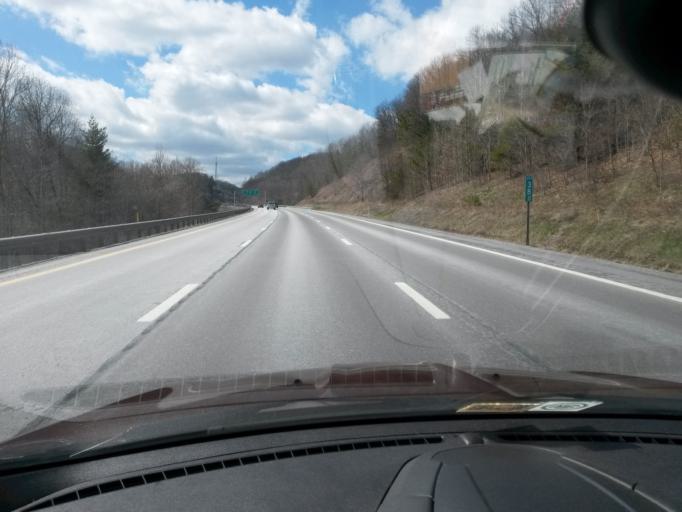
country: US
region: West Virginia
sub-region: Raleigh County
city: Beaver
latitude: 37.7210
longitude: -81.1707
